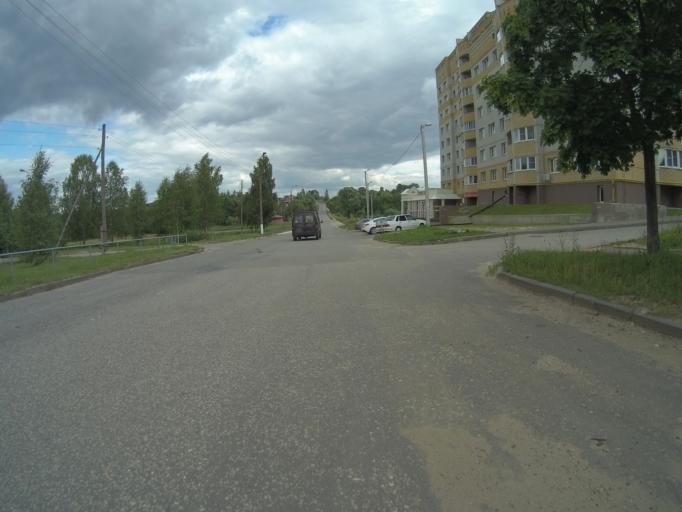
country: RU
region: Vladimir
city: Kommunar
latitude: 56.0623
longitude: 40.4871
